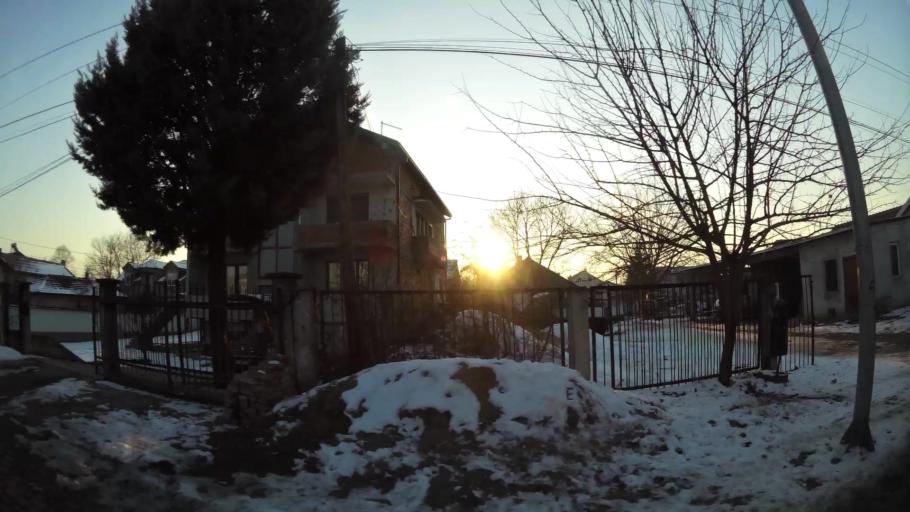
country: MK
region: Kisela Voda
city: Kisela Voda
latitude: 41.9756
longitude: 21.4859
